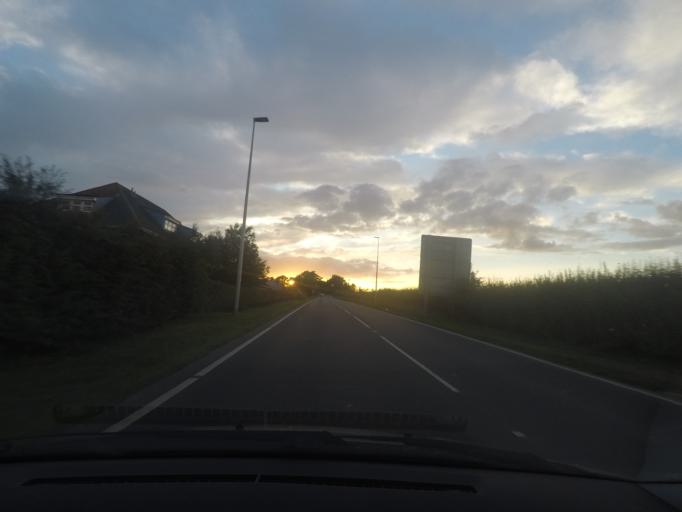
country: GB
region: England
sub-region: North Lincolnshire
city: Croxton
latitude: 53.5850
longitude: -0.3527
